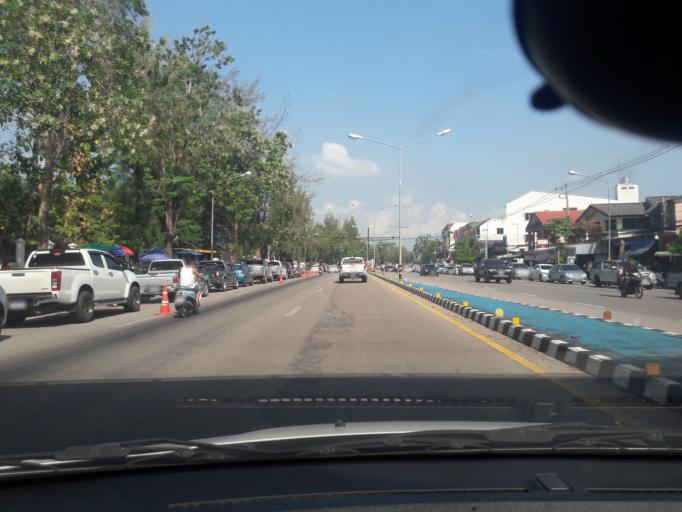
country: TH
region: Lampang
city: Lampang
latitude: 18.2357
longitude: 99.4905
